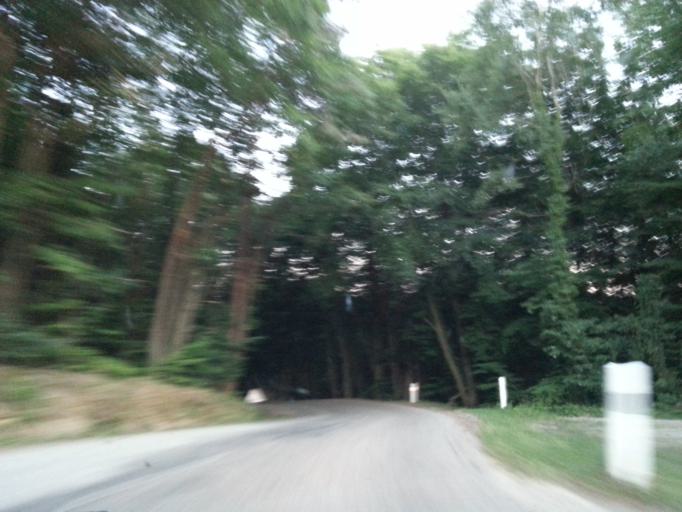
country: FR
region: Alsace
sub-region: Departement du Bas-Rhin
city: Lembach
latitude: 48.9914
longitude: 7.8456
